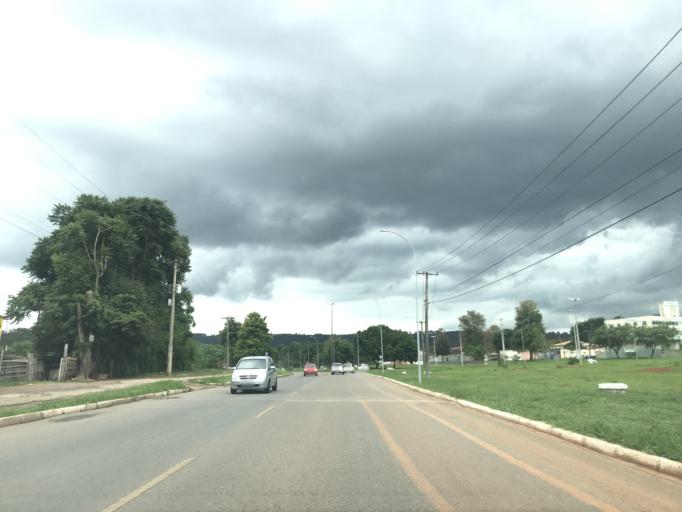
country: BR
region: Federal District
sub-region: Brasilia
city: Brasilia
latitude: -15.6470
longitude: -47.8118
